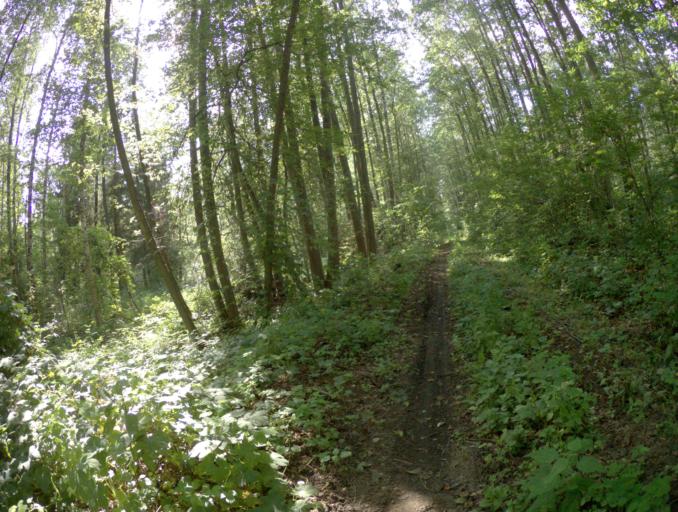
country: RU
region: Vladimir
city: Sobinka
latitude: 55.9092
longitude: 40.1258
